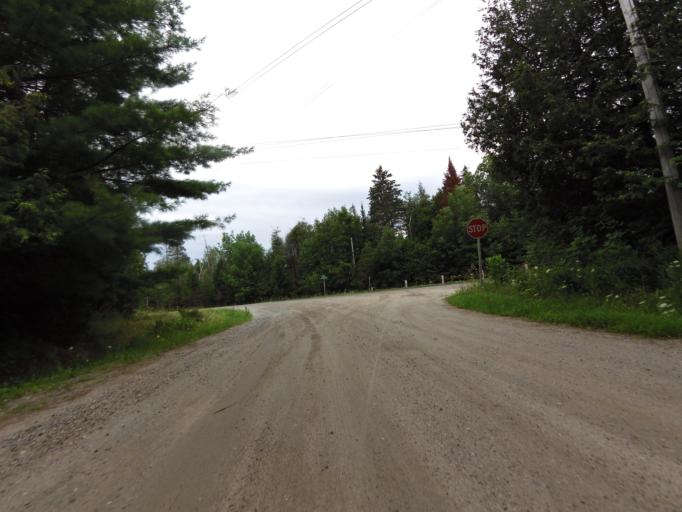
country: CA
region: Ontario
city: Perth
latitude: 45.0402
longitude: -76.3950
